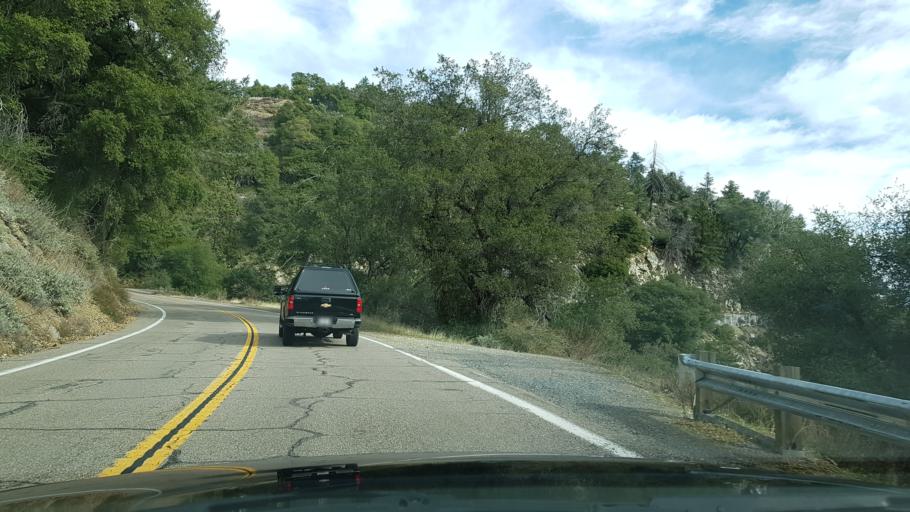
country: US
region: California
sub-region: Riverside County
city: Aguanga
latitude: 33.3045
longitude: -116.8760
